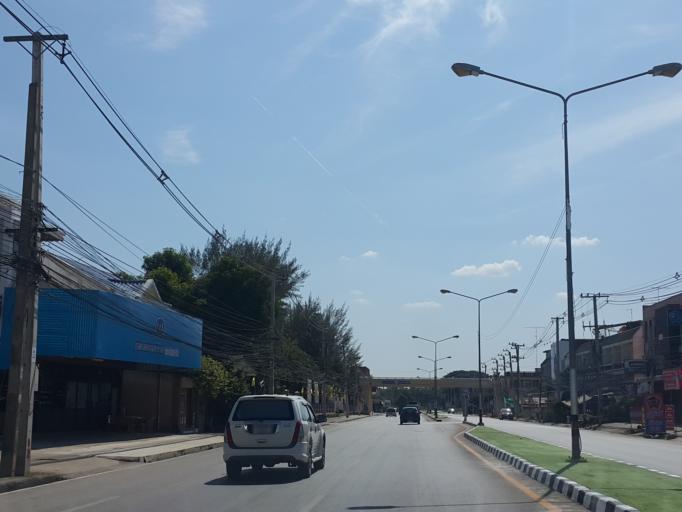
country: TH
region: Sukhothai
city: Sawankhalok
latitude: 17.2971
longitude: 99.8361
